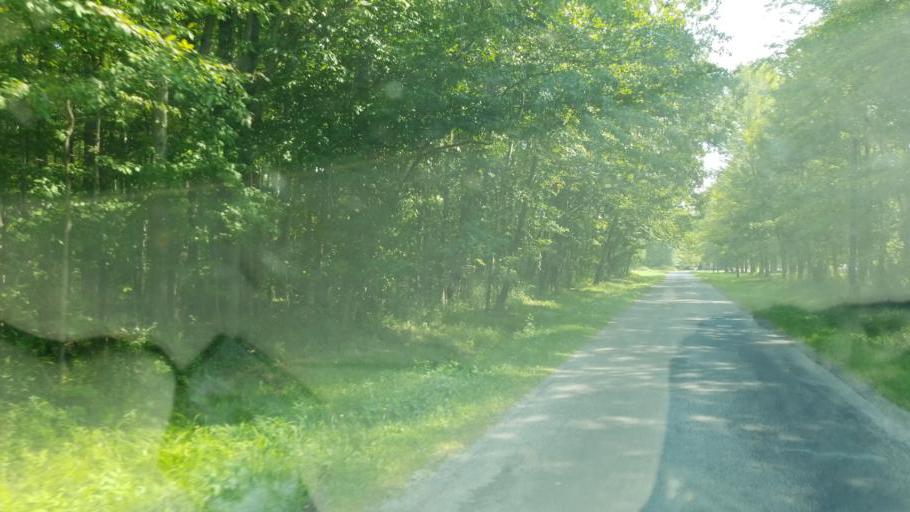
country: US
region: Ohio
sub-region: Lake County
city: Madison
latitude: 41.6332
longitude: -80.9948
